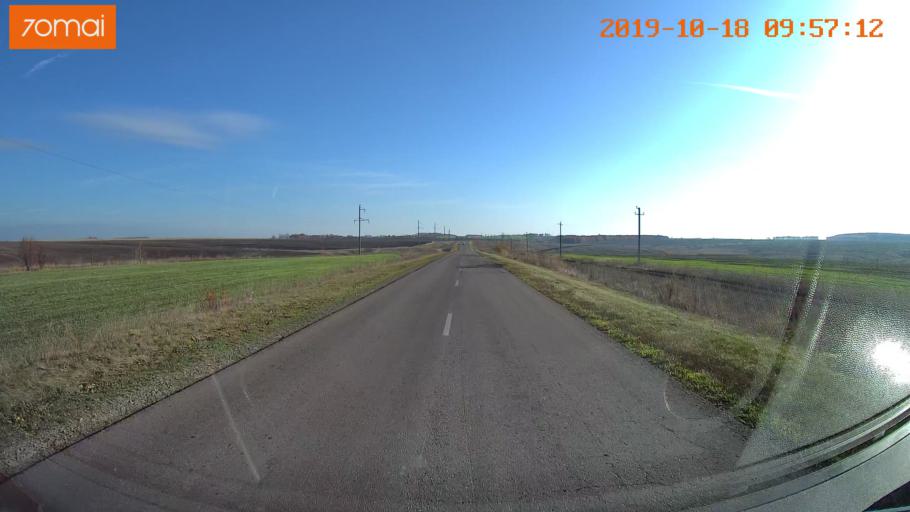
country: RU
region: Tula
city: Kurkino
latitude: 53.3764
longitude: 38.4100
